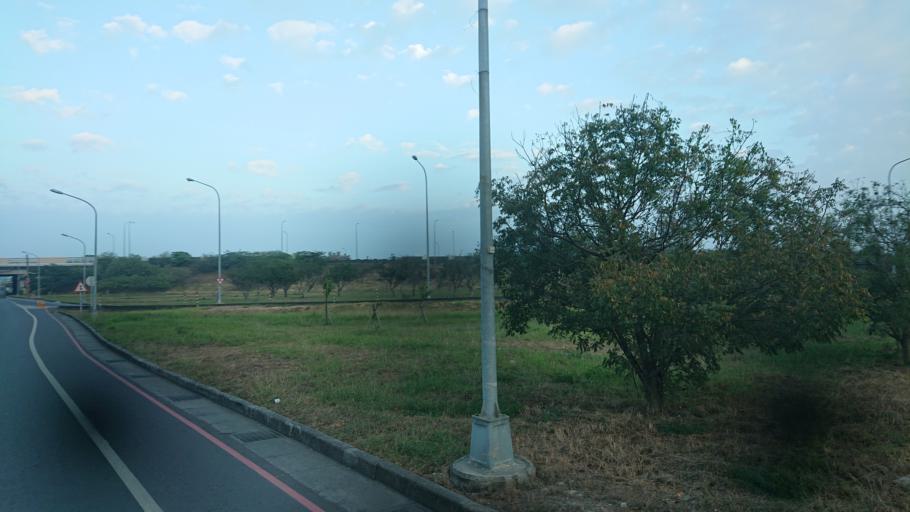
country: TW
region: Taiwan
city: Xinying
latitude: 23.1813
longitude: 120.2335
